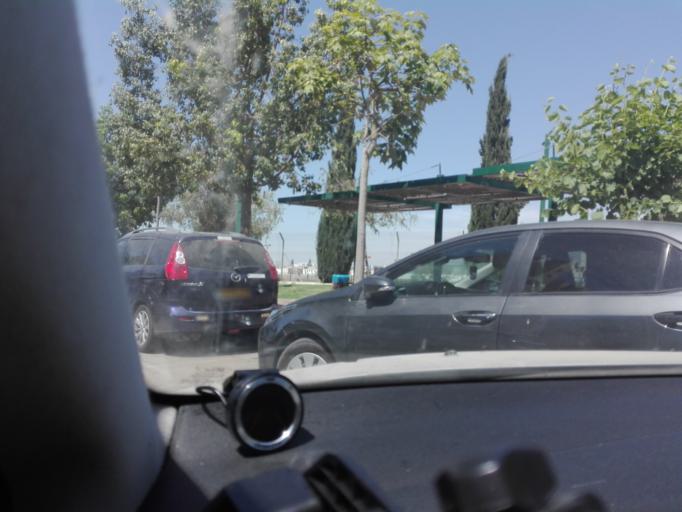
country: IL
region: Central District
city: Bene 'Ayish
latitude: 31.7333
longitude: 34.7374
